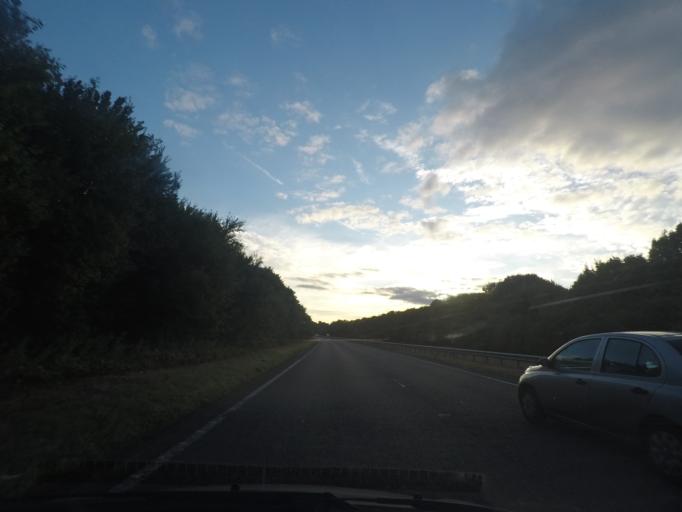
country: GB
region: England
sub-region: Oxfordshire
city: Frilford
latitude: 51.6829
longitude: -1.4288
